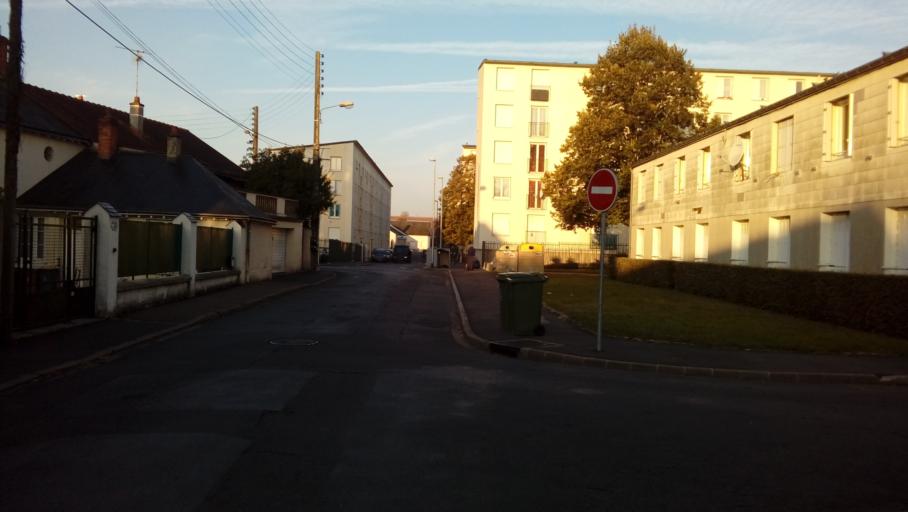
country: FR
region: Centre
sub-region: Departement du Loiret
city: Saint-Jean-le-Blanc
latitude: 47.9109
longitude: 1.9286
